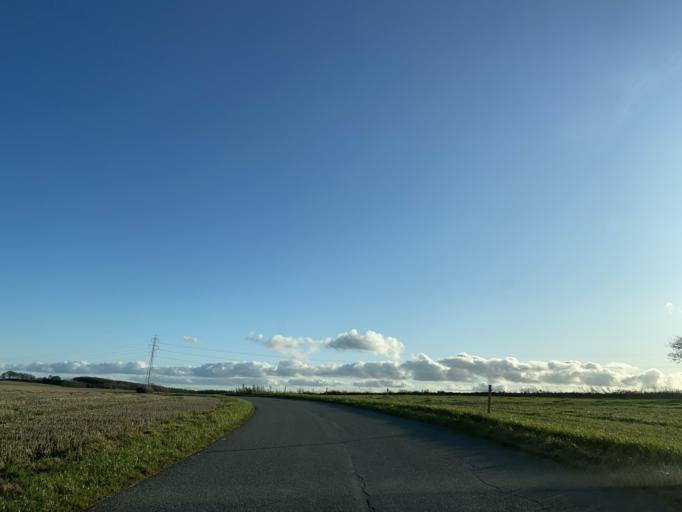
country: DK
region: Central Jutland
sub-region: Viborg Kommune
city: Bjerringbro
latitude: 56.3515
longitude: 9.7172
